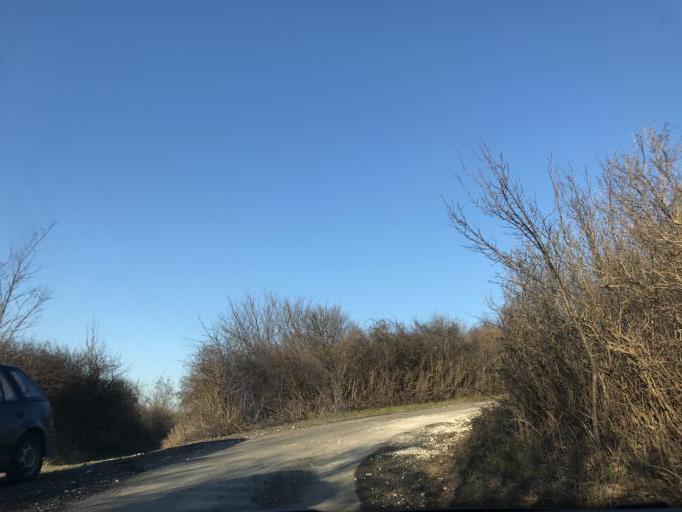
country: HU
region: Komarom-Esztergom
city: Csolnok
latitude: 47.6440
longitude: 18.7393
